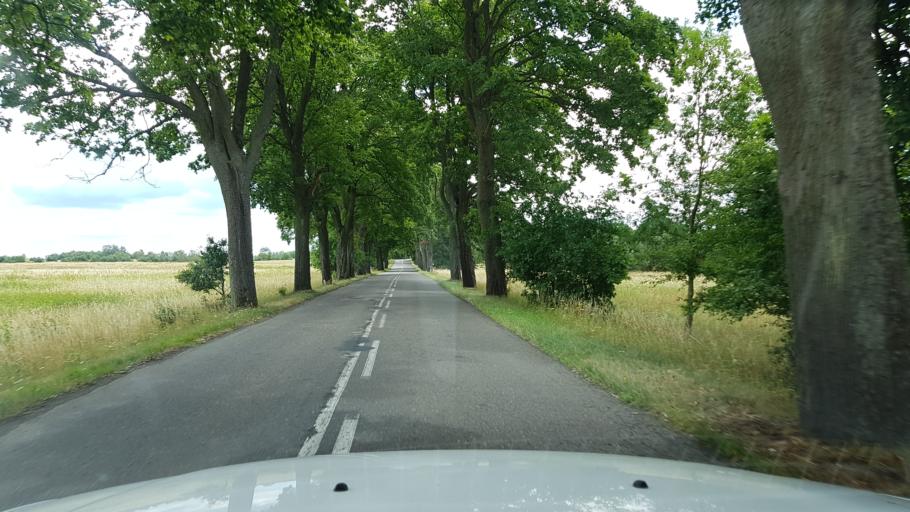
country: PL
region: West Pomeranian Voivodeship
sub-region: Powiat stargardzki
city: Insko
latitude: 53.3888
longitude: 15.5760
